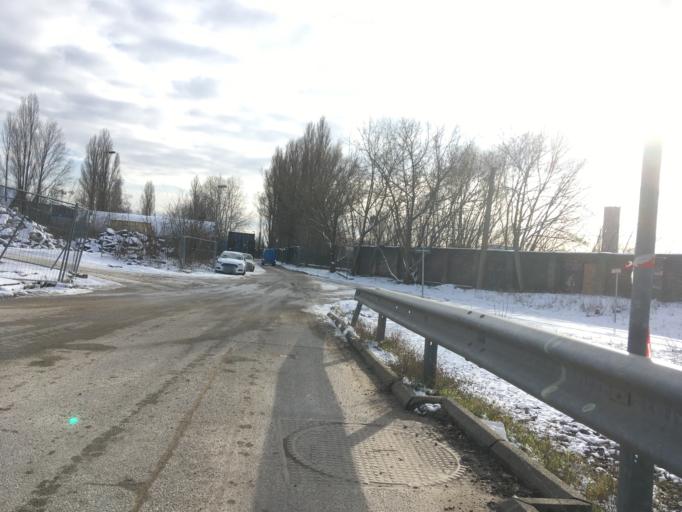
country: DE
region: Berlin
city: Rummelsburg
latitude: 52.4868
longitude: 13.5047
